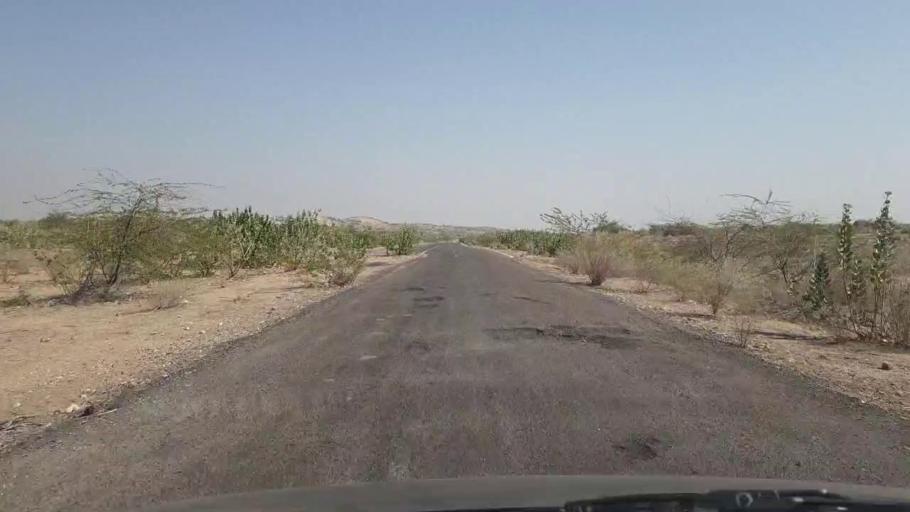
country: PK
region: Sindh
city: Chor
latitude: 25.5678
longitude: 69.8986
